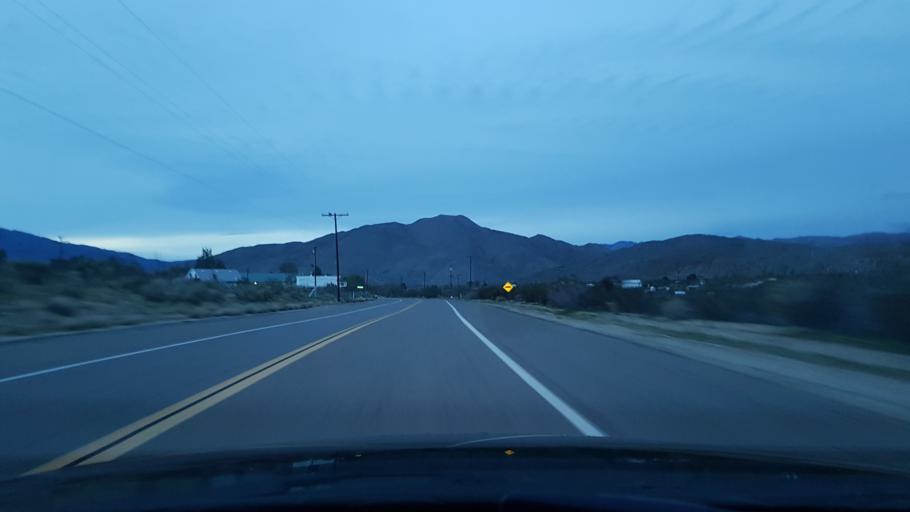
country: US
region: California
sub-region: San Diego County
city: Julian
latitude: 33.0754
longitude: -116.4361
